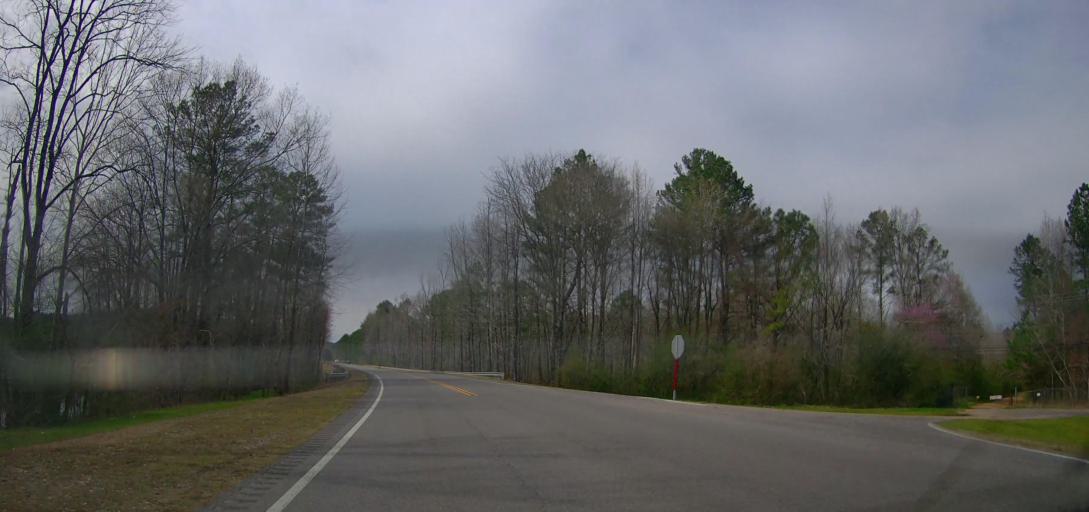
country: US
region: Alabama
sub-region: Walker County
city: Carbon Hill
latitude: 33.8974
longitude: -87.5381
